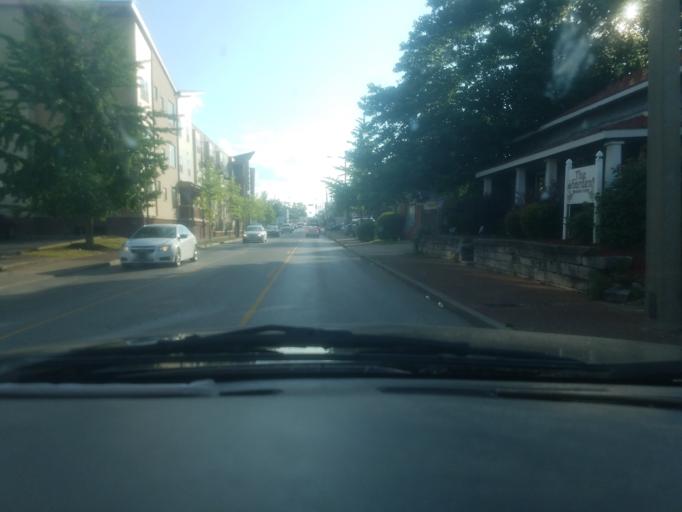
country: US
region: Tennessee
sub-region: Davidson County
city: Nashville
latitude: 36.1728
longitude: -86.7936
